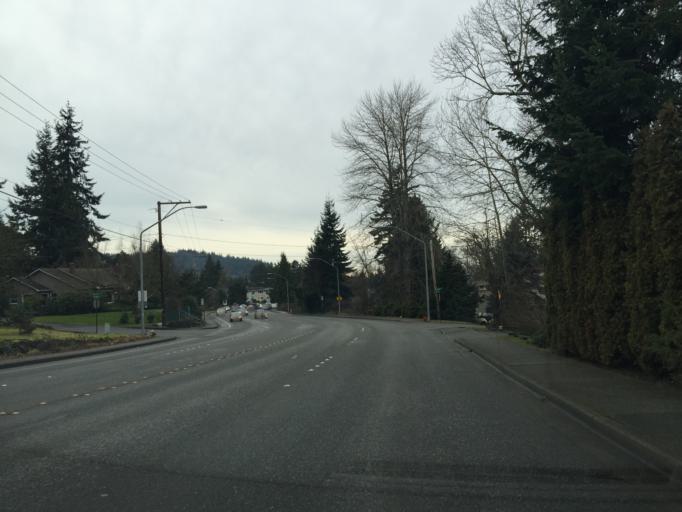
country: US
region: Washington
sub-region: Whatcom County
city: Bellingham
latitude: 48.7453
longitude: -122.4529
